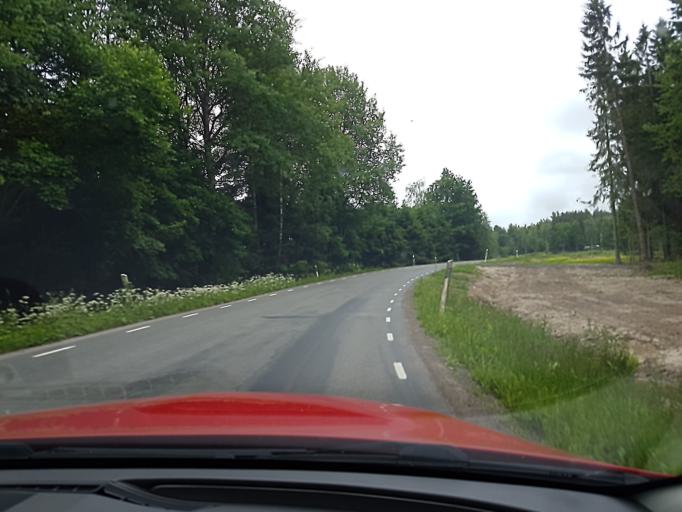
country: SE
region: Vaestra Goetaland
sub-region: Tidaholms Kommun
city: Olofstorp
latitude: 58.3572
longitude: 13.9585
